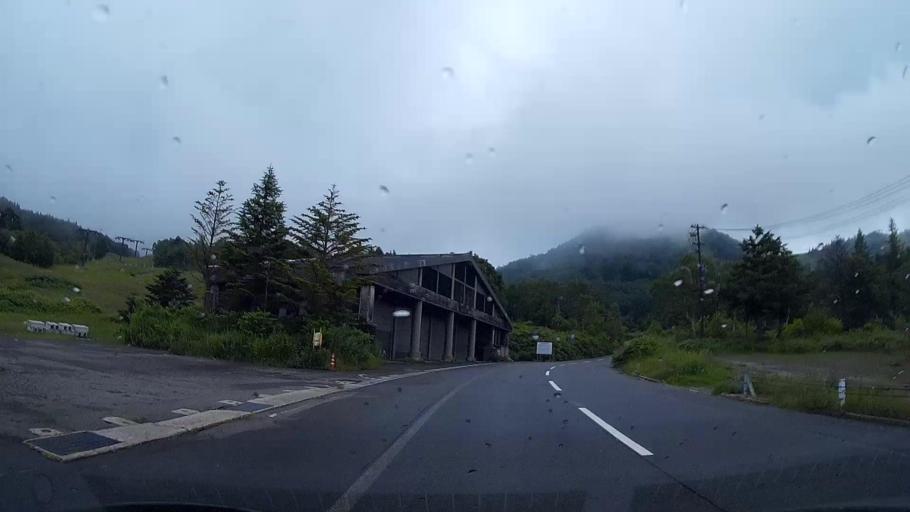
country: JP
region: Nagano
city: Nakano
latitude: 36.6830
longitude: 138.4996
